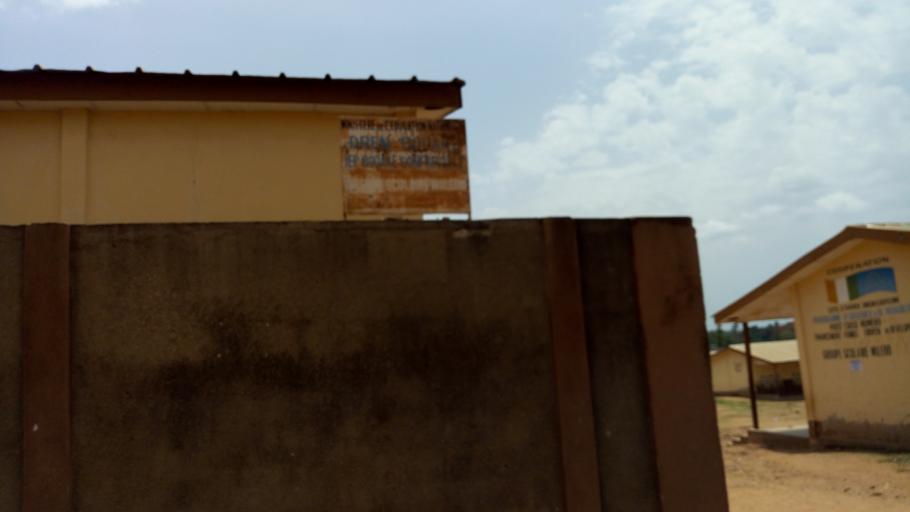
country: CI
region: Vallee du Bandama
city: Bouake
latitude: 7.7176
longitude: -5.0456
